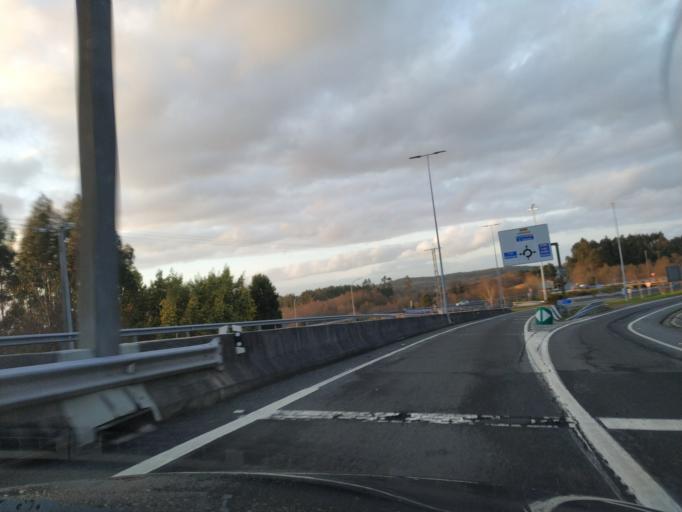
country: ES
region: Galicia
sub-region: Provincia da Coruna
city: Oroso
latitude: 42.9085
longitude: -8.4322
